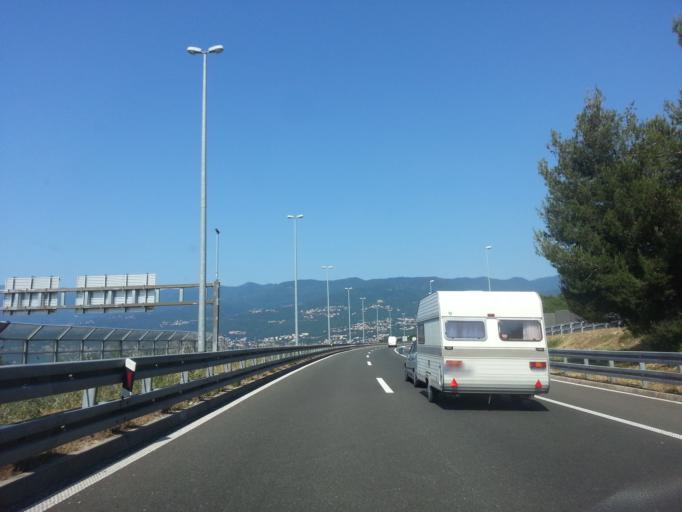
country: HR
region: Primorsko-Goranska
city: Rubesi
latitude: 45.3483
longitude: 14.3699
